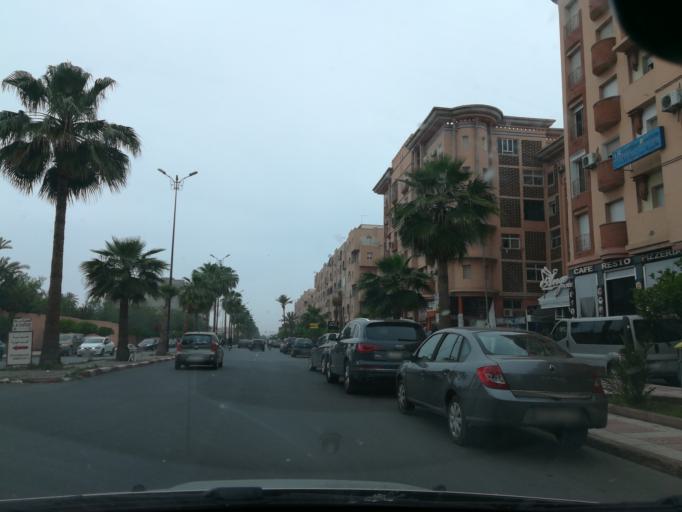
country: MA
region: Marrakech-Tensift-Al Haouz
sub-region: Marrakech
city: Marrakesh
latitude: 31.6586
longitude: -8.0055
